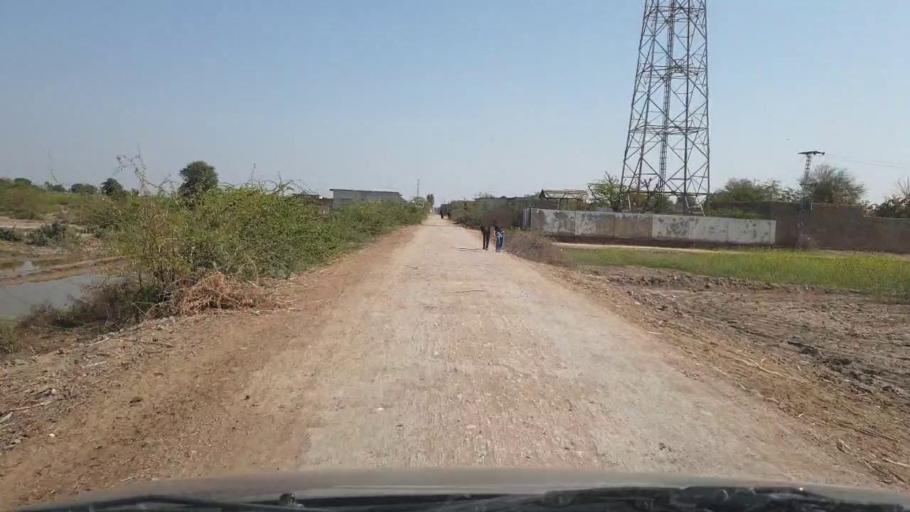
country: PK
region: Sindh
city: Samaro
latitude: 25.2450
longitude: 69.2441
